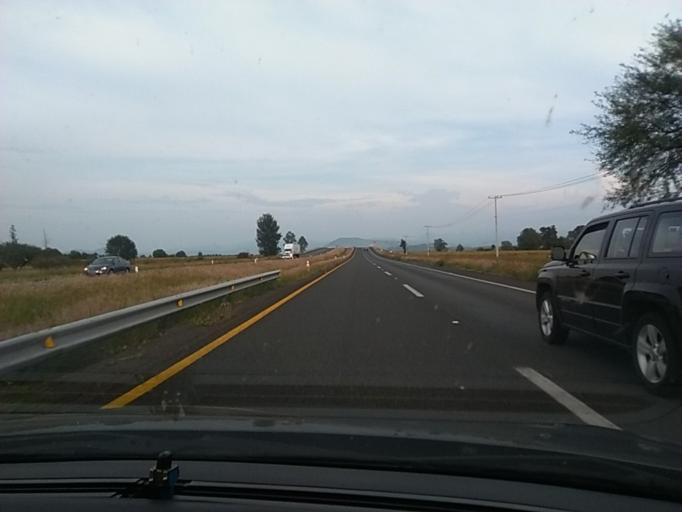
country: MX
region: Michoacan
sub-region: Alvaro Obregon
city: Tzintzimeo
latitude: 19.8909
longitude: -100.9810
